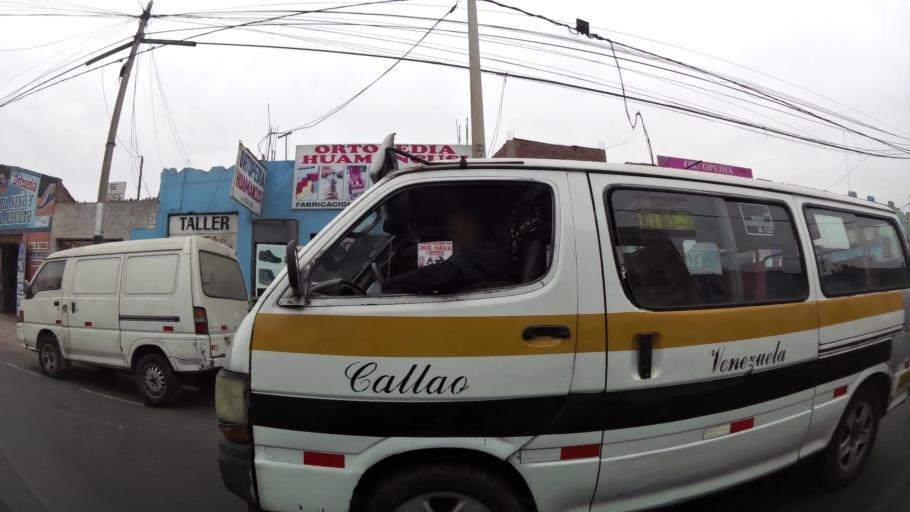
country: PE
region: Callao
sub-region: Callao
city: Callao
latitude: -12.0625
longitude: -77.1338
